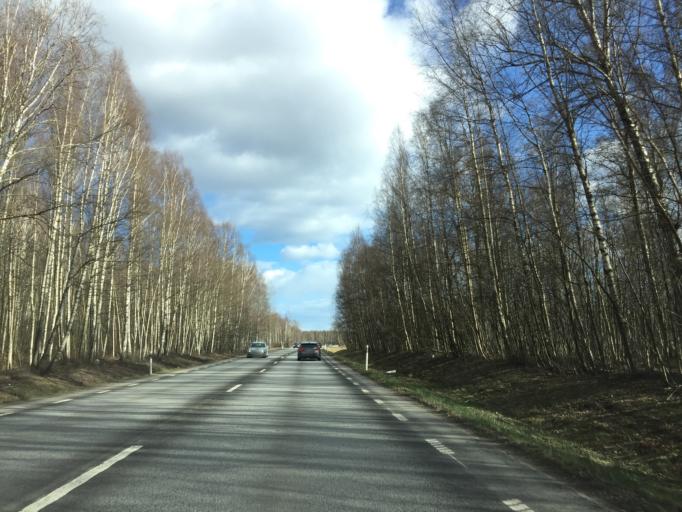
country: SE
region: OErebro
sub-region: Kumla Kommun
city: Kumla
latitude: 59.1636
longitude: 15.1194
